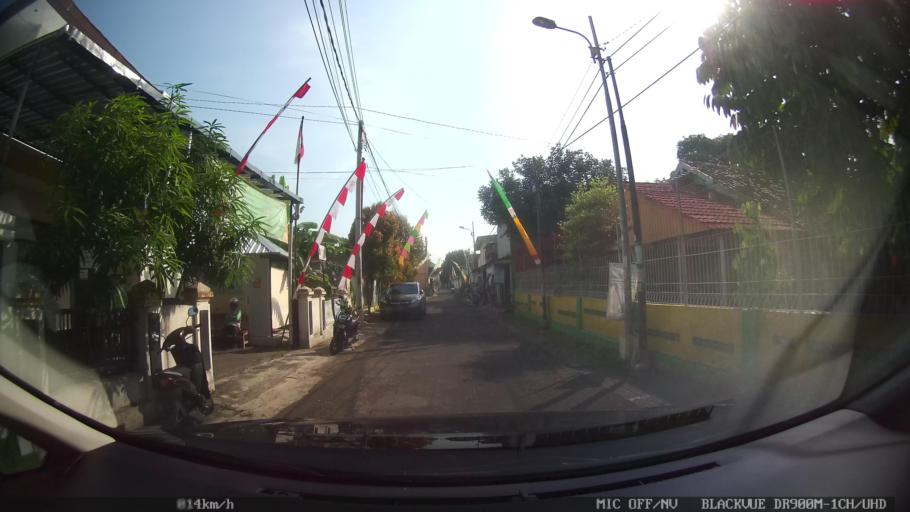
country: ID
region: Daerah Istimewa Yogyakarta
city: Yogyakarta
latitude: -7.7841
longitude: 110.3550
